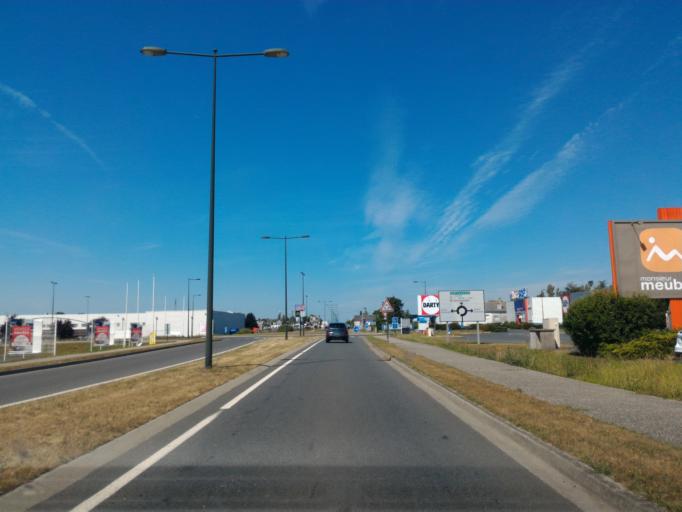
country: FR
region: Centre
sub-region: Departement de l'Indre
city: Saint-Maur
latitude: 46.7811
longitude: 1.6535
